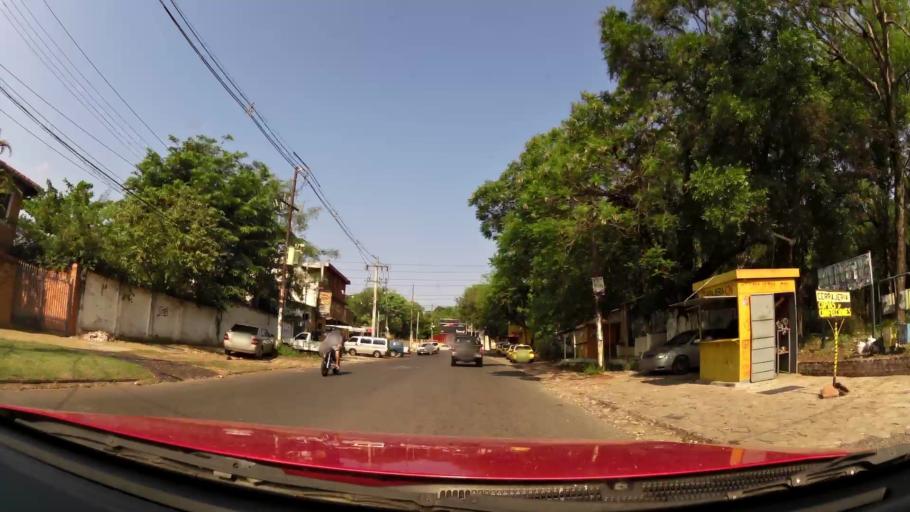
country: PY
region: Asuncion
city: Asuncion
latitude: -25.3177
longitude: -57.6304
